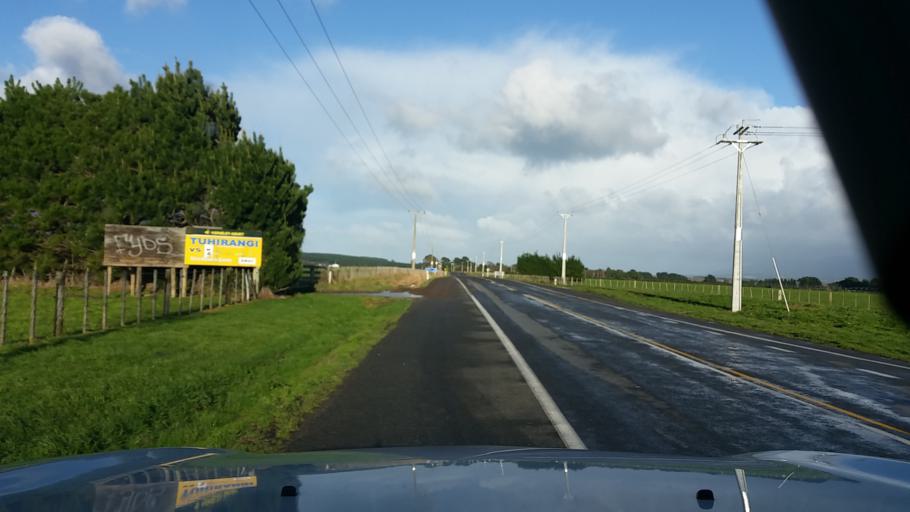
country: NZ
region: Wellington
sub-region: South Wairarapa District
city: Waipawa
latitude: -41.3060
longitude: 175.2737
